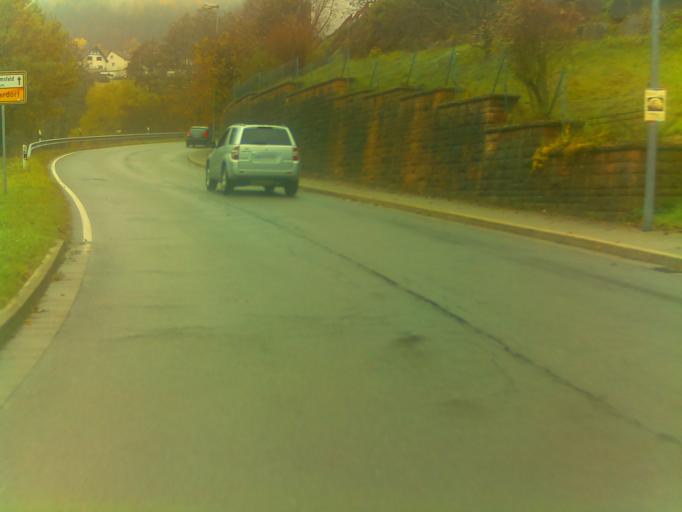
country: DE
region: Baden-Wuerttemberg
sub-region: Karlsruhe Region
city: Wilhelmsfeld
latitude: 49.4664
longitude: 8.7710
